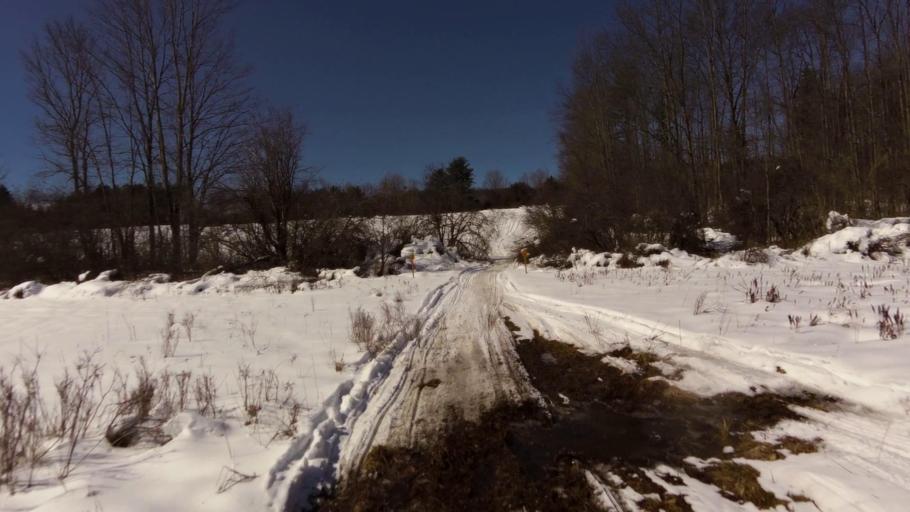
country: US
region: New York
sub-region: Allegany County
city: Houghton
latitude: 42.3618
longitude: -78.1554
